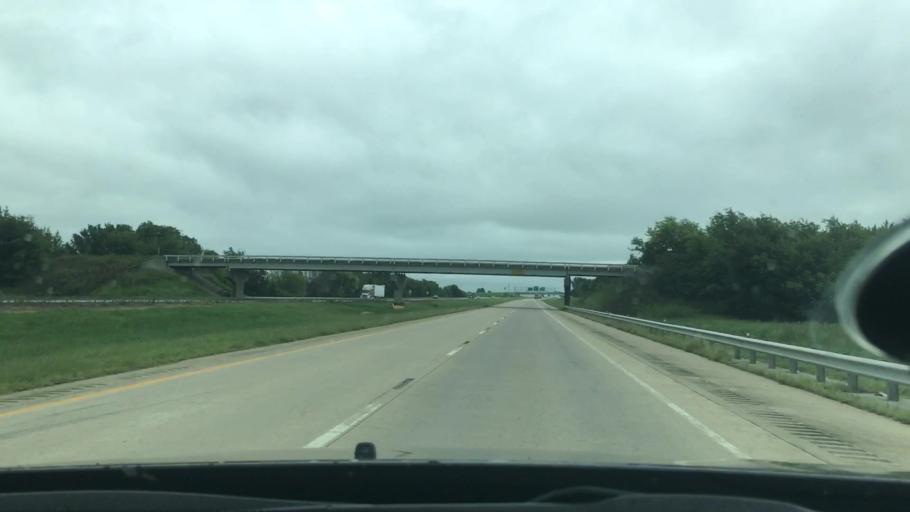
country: US
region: Oklahoma
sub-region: McIntosh County
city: Checotah
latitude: 35.4579
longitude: -95.5587
